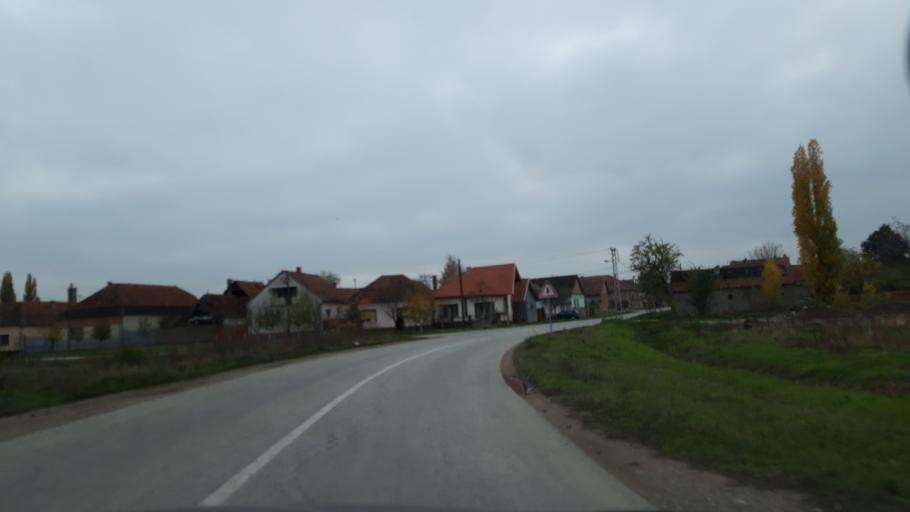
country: RS
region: Autonomna Pokrajina Vojvodina
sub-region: Severnobanatski Okrug
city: Novi Knezevac
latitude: 46.0458
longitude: 20.1037
